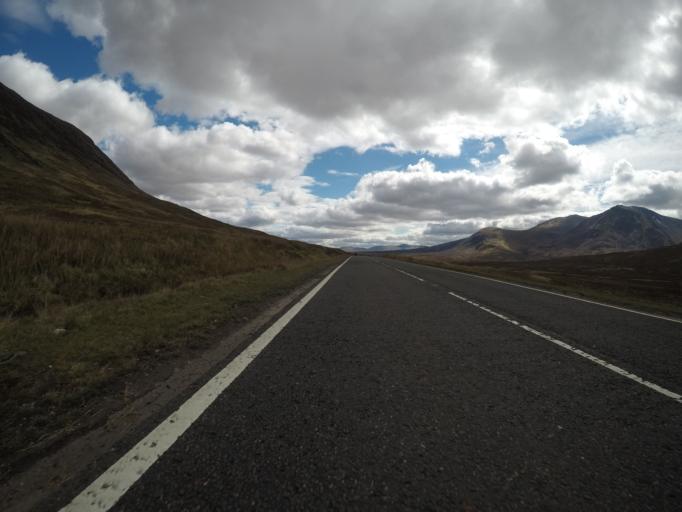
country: GB
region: Scotland
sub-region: Highland
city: Spean Bridge
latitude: 56.6602
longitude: -4.8871
